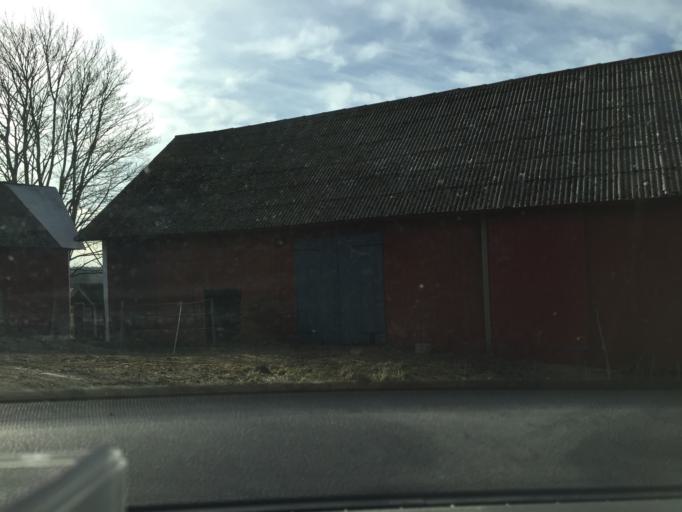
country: SE
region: OErebro
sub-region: Hallsbergs Kommun
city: Skollersta
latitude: 59.1366
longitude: 15.4093
